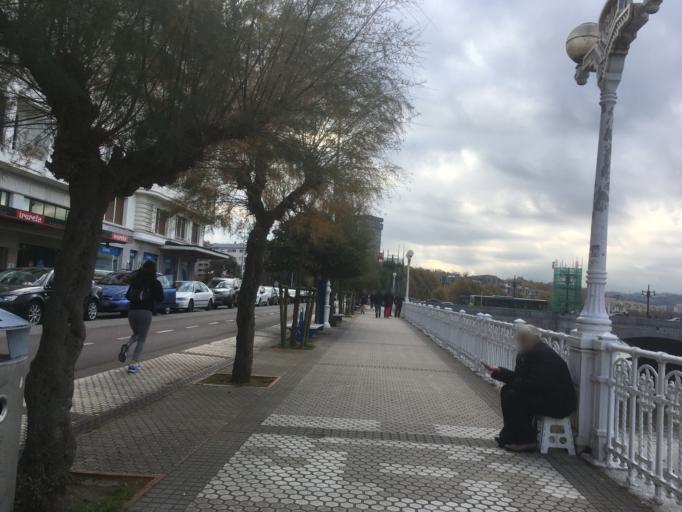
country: ES
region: Basque Country
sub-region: Provincia de Guipuzcoa
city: San Sebastian
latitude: 43.3218
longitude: -1.9781
